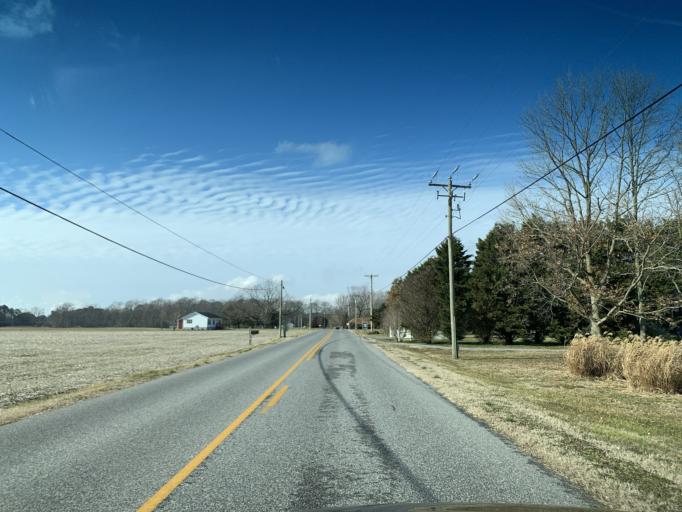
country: US
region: Maryland
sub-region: Worcester County
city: Ocean Pines
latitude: 38.4204
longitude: -75.1557
